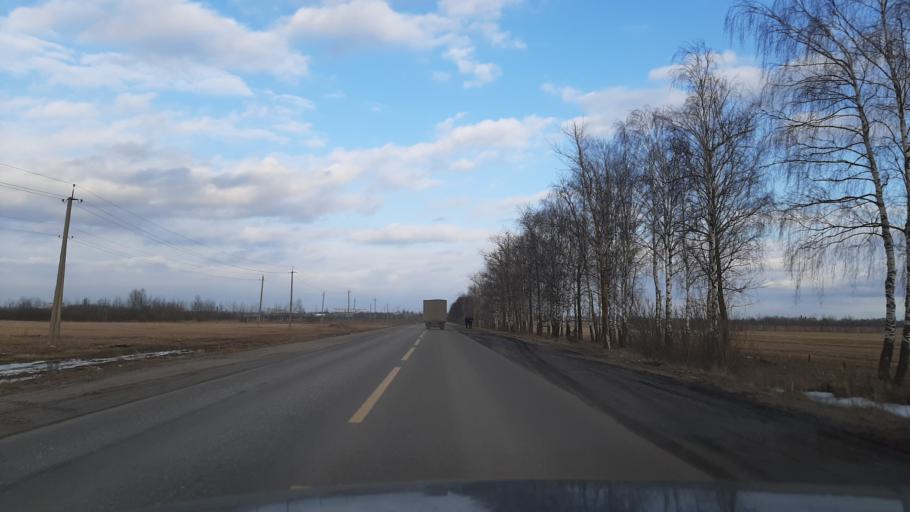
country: RU
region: Ivanovo
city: Novo-Talitsy
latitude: 56.9841
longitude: 40.8798
